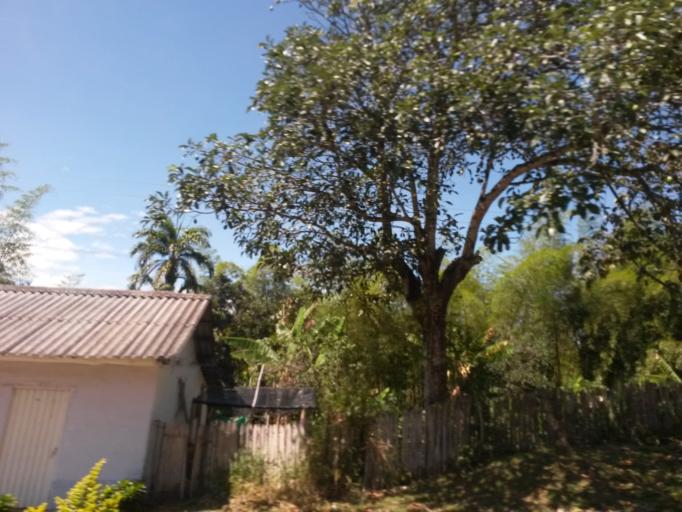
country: CO
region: Cauca
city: El Tambo
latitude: 2.4496
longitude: -76.8038
